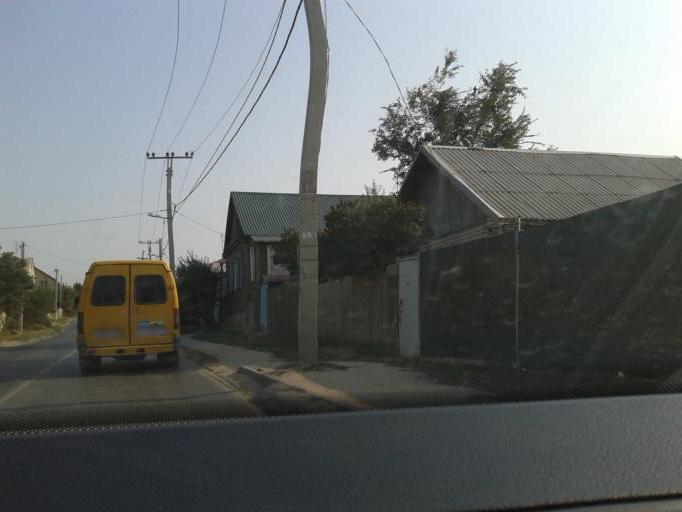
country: RU
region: Volgograd
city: Volgograd
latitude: 48.6962
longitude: 44.4478
